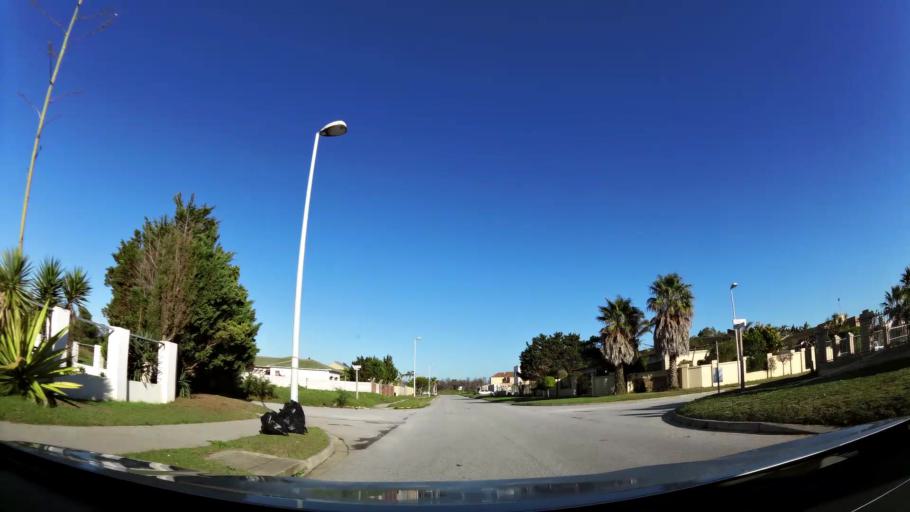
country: ZA
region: Eastern Cape
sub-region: Nelson Mandela Bay Metropolitan Municipality
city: Port Elizabeth
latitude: -34.0025
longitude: 25.6532
